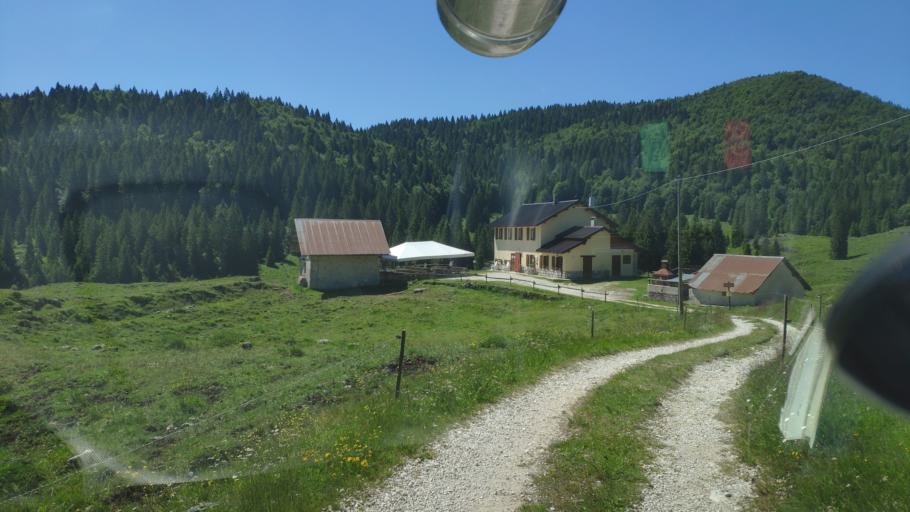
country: IT
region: Veneto
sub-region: Provincia di Vicenza
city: Caltrano
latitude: 45.8078
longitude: 11.4577
